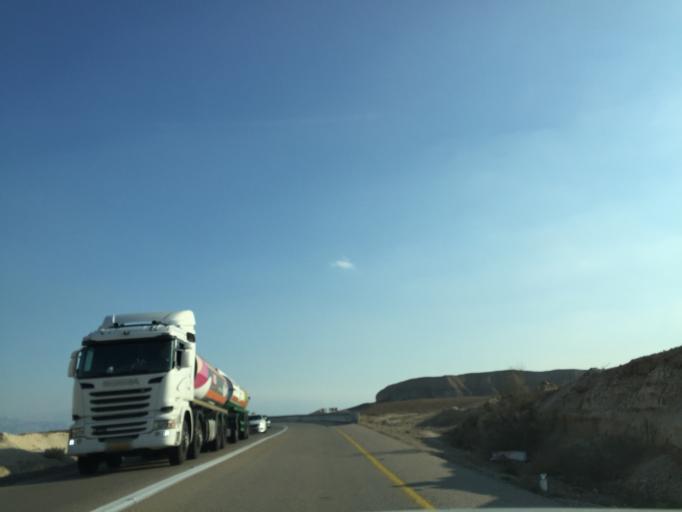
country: IL
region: Southern District
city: `En Boqeq
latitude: 31.1689
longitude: 35.3167
